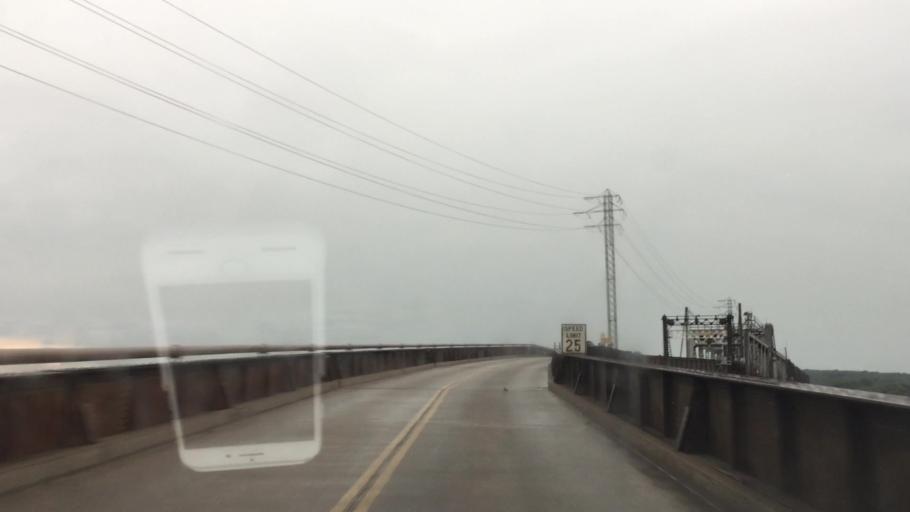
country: US
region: Iowa
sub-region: Lee County
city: Fort Madison
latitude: 40.6296
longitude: -91.2990
